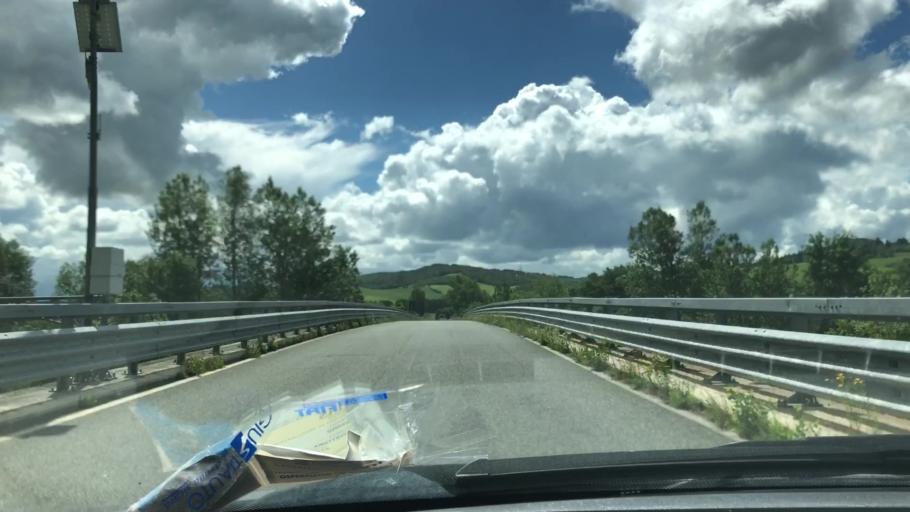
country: IT
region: Tuscany
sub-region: Province of Pisa
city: Saline
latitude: 43.3548
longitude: 10.7851
